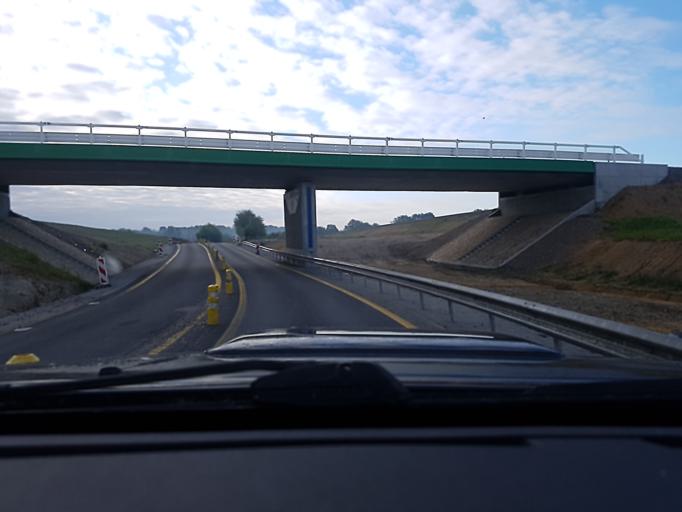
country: FR
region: Pays de la Loire
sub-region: Departement de la Vendee
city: Aizenay
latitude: 46.7577
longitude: -1.6425
